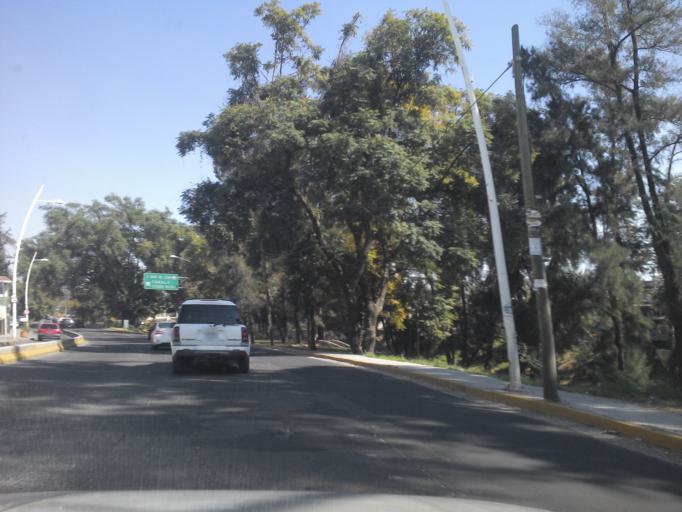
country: MX
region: Jalisco
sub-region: Zapopan
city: Zapopan
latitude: 20.7063
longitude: -103.3622
